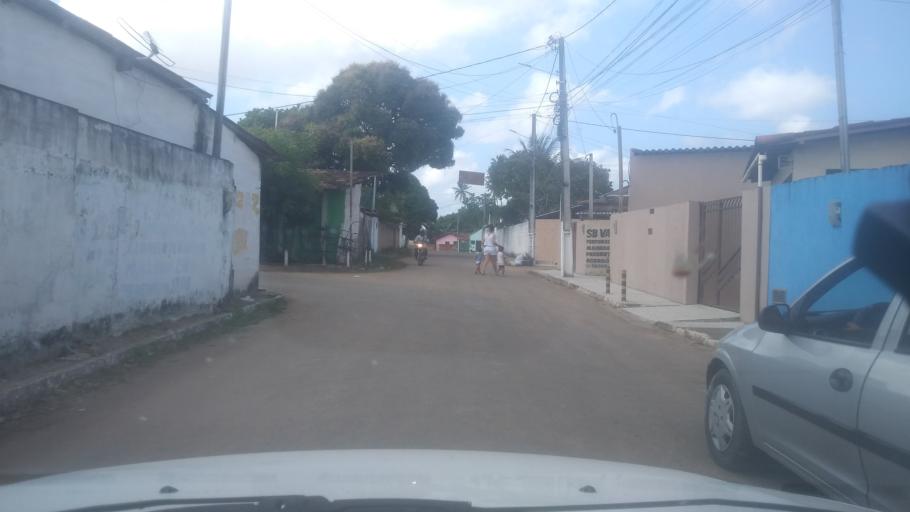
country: BR
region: Rio Grande do Norte
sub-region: Extremoz
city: Extremoz
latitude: -5.7070
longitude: -35.3066
